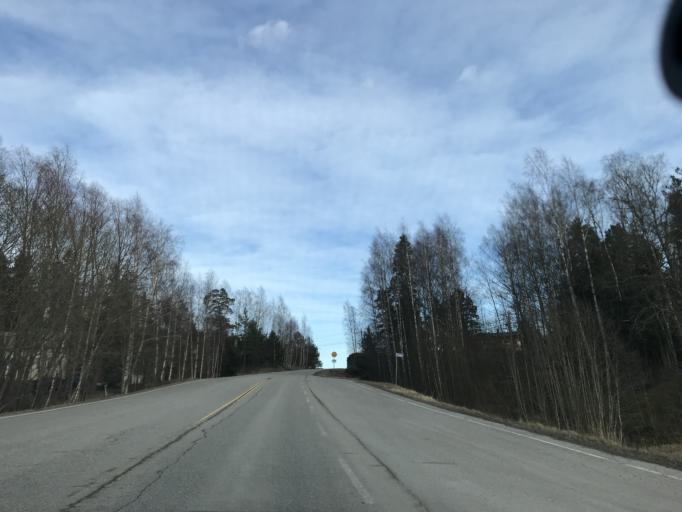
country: FI
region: Uusimaa
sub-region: Raaseporin
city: Pohja
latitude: 60.0918
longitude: 23.4818
